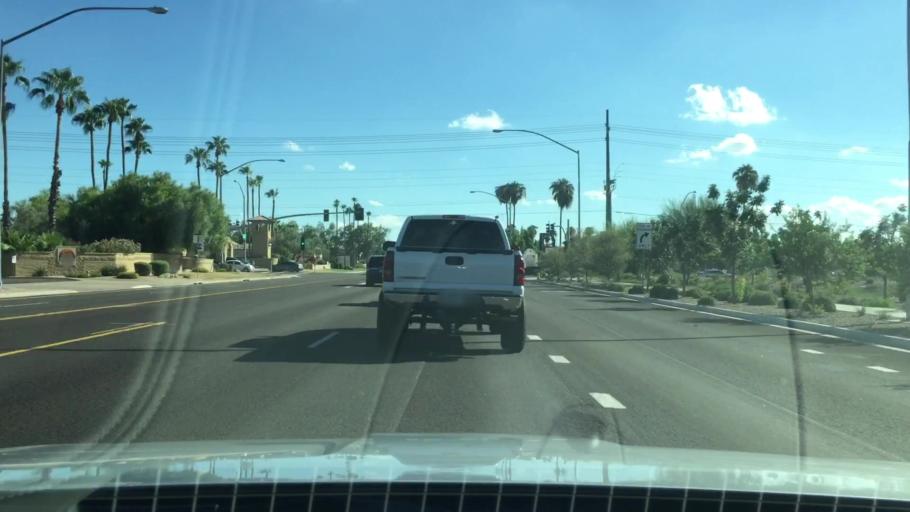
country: US
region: Arizona
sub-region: Maricopa County
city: Mesa
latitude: 33.4384
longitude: -111.7191
